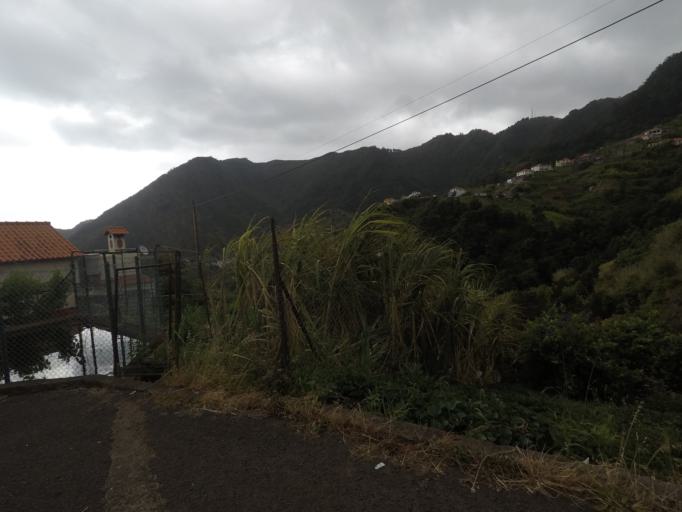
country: PT
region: Madeira
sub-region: Santana
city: Santana
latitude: 32.7569
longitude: -16.8274
